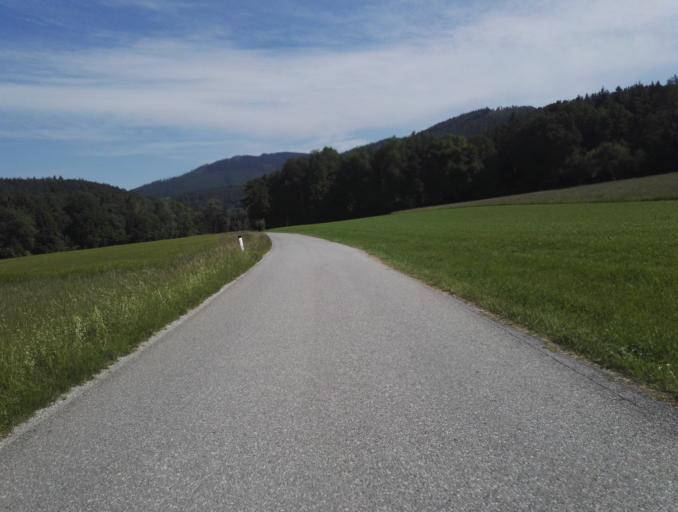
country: AT
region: Styria
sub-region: Politischer Bezirk Graz-Umgebung
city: Stattegg
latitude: 47.1484
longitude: 15.4342
